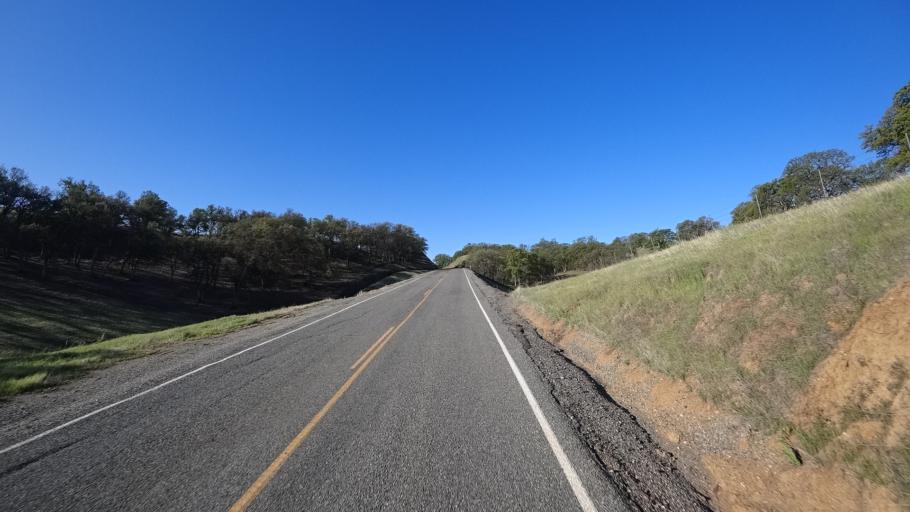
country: US
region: California
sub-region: Tehama County
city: Rancho Tehama Reserve
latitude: 39.8215
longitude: -122.3808
